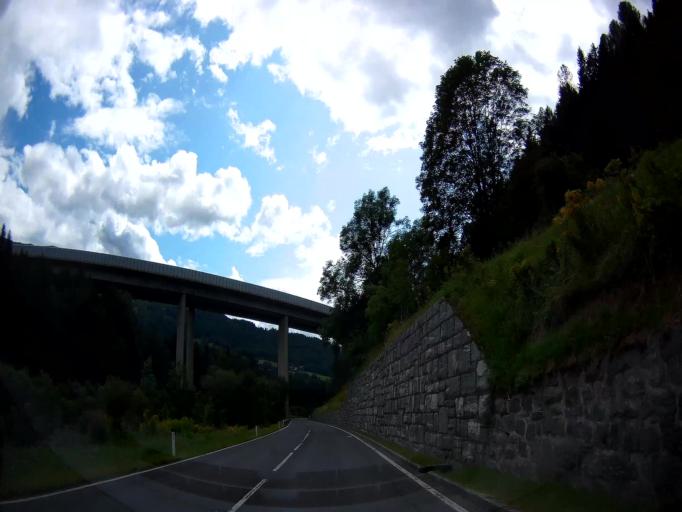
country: AT
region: Carinthia
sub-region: Politischer Bezirk Spittal an der Drau
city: Gmuend
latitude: 46.9009
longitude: 13.5292
